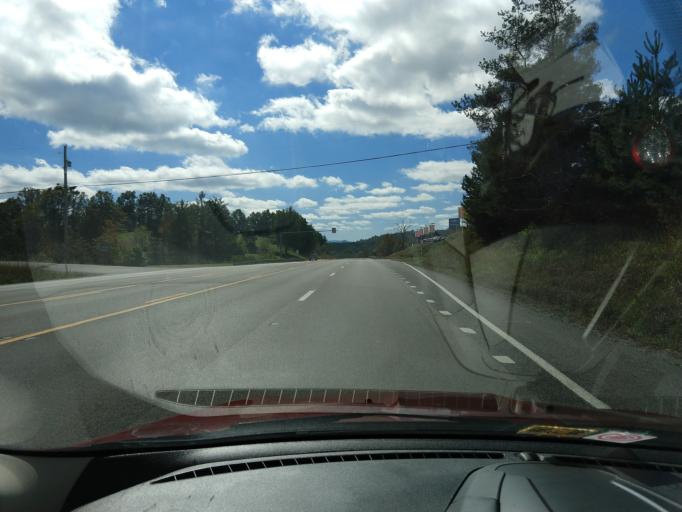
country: US
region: West Virginia
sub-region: Randolph County
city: Elkins
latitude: 38.8734
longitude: -79.8421
